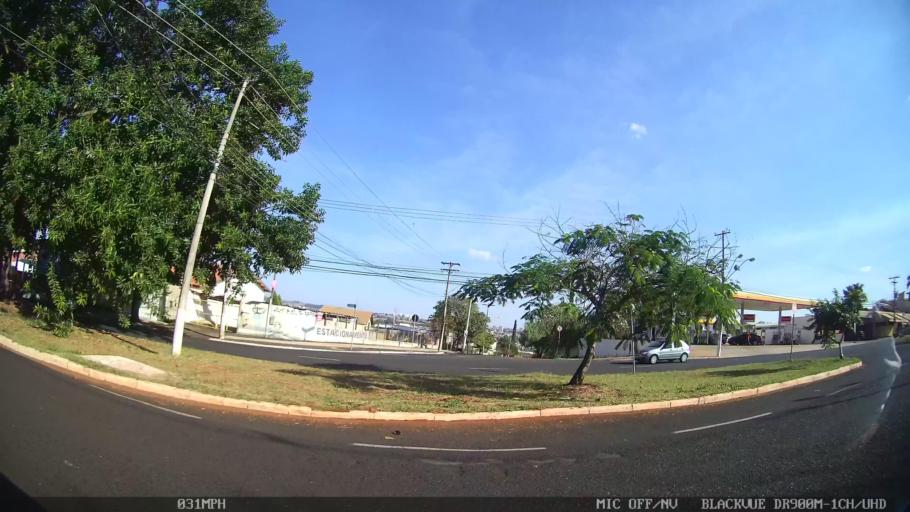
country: BR
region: Sao Paulo
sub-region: Ribeirao Preto
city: Ribeirao Preto
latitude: -21.2039
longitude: -47.7774
